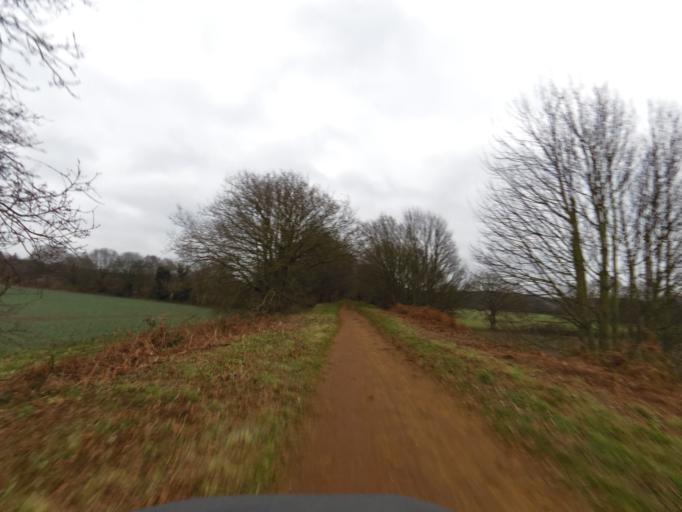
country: GB
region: England
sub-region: Norfolk
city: Costessey
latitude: 52.7110
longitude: 1.1605
